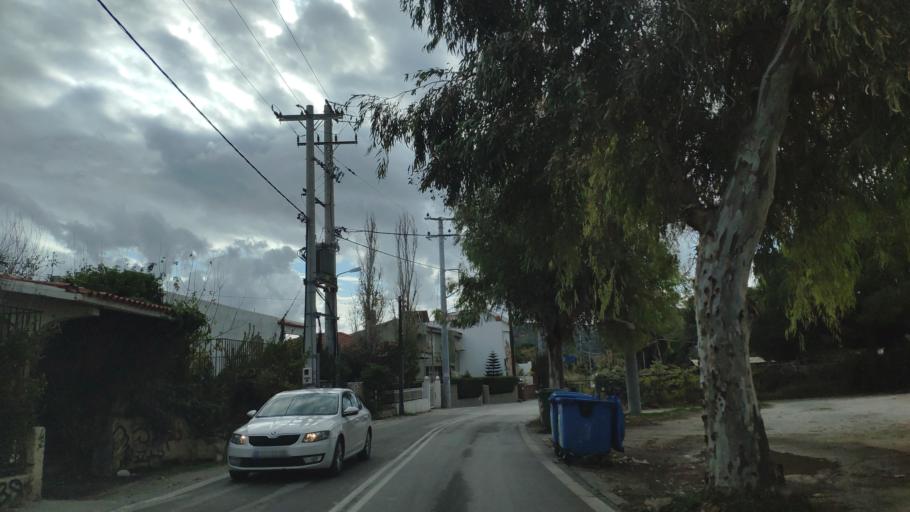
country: GR
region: Attica
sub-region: Nomarchia Anatolikis Attikis
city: Artemida
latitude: 37.9342
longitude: 24.0119
